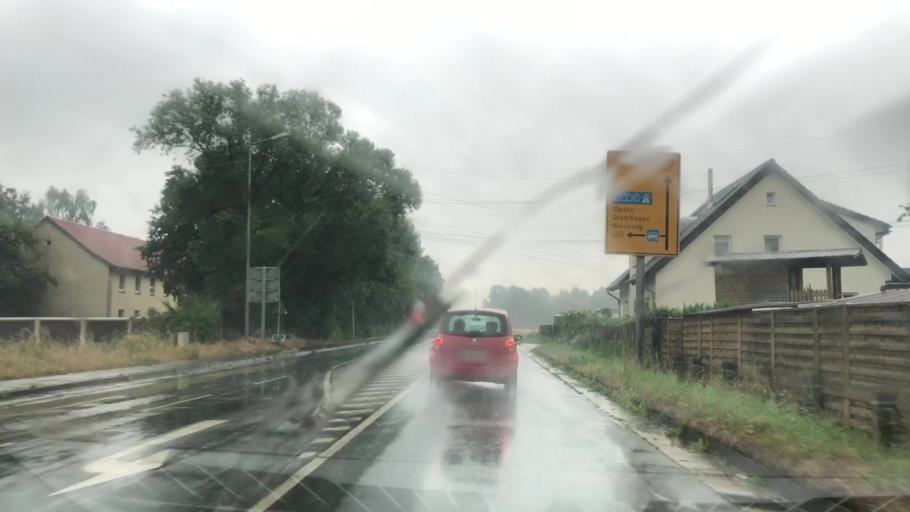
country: DE
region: North Rhine-Westphalia
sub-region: Regierungsbezirk Detmold
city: Minden
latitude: 52.2778
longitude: 8.9621
